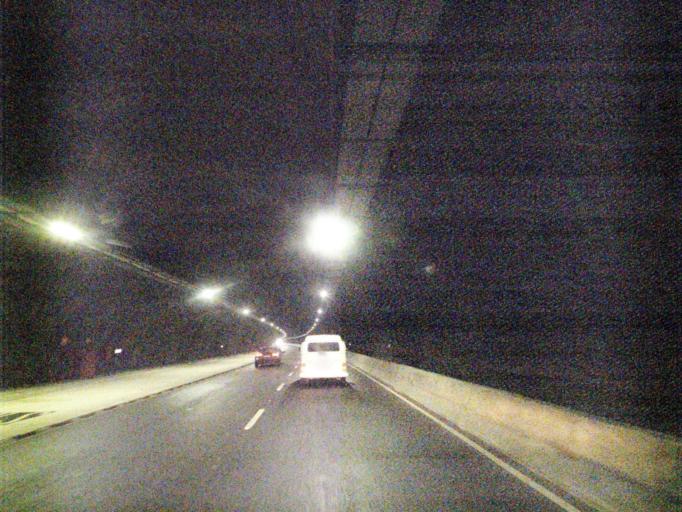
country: BR
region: Rio de Janeiro
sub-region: Niteroi
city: Niteroi
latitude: -22.9354
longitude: -43.0889
